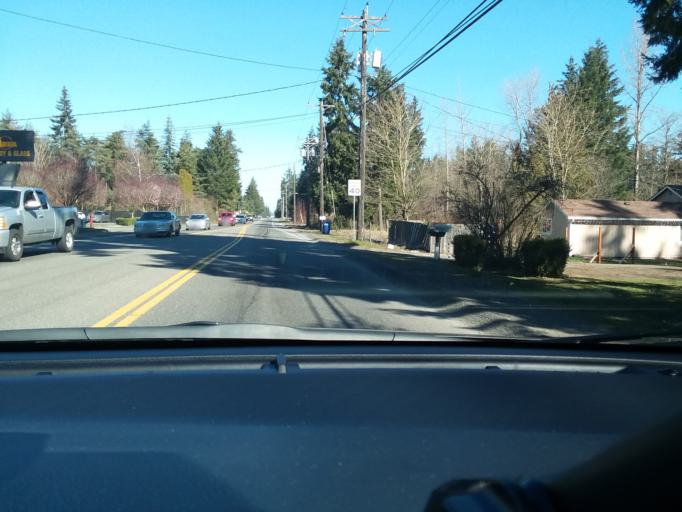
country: US
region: Washington
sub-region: Pierce County
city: Summit
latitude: 47.1814
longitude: -122.3572
